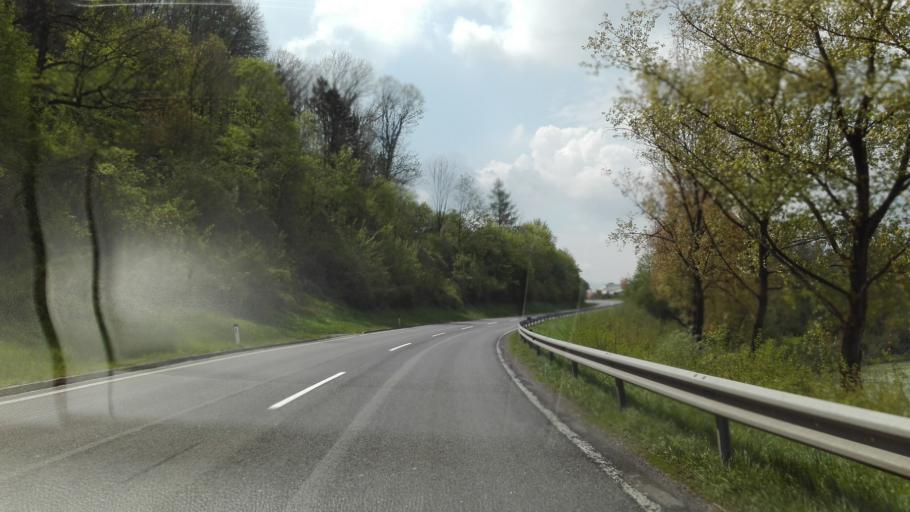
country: AT
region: Upper Austria
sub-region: Politischer Bezirk Steyr-Land
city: Sankt Ulrich bei Steyr
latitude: 48.0193
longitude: 14.4174
